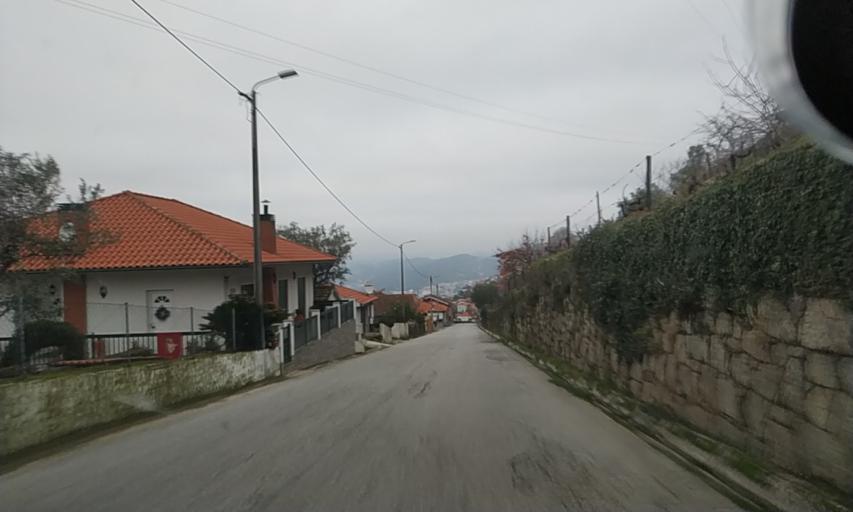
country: PT
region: Viseu
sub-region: Lamego
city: Lamego
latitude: 41.1225
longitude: -7.8028
